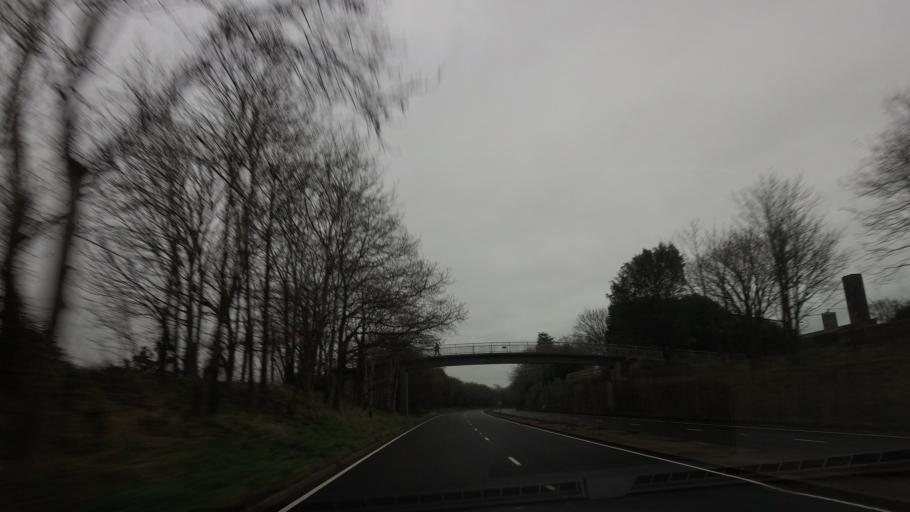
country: GB
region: England
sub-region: East Sussex
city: Bexhill-on-Sea
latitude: 50.8470
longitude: 0.4782
